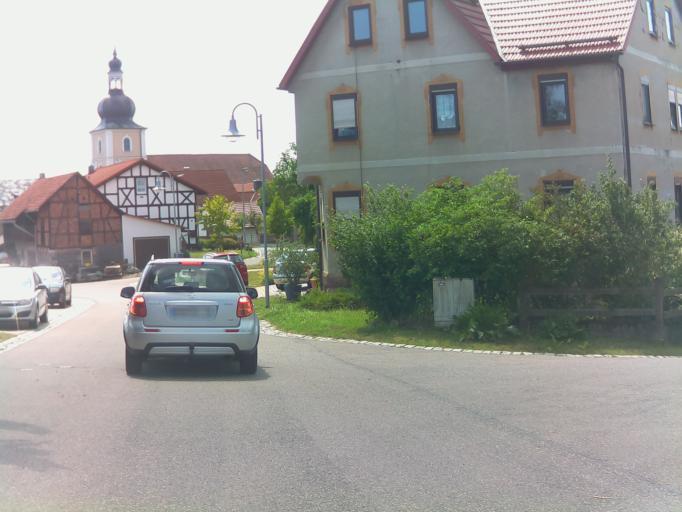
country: DE
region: Thuringia
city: Hildburghausen
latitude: 50.3757
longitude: 10.7397
